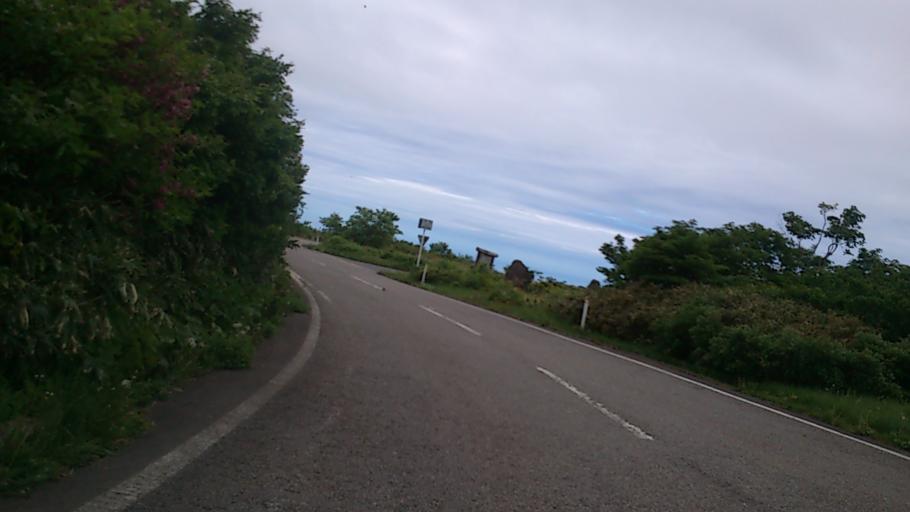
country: JP
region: Yamagata
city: Yuza
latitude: 39.1071
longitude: 139.9782
